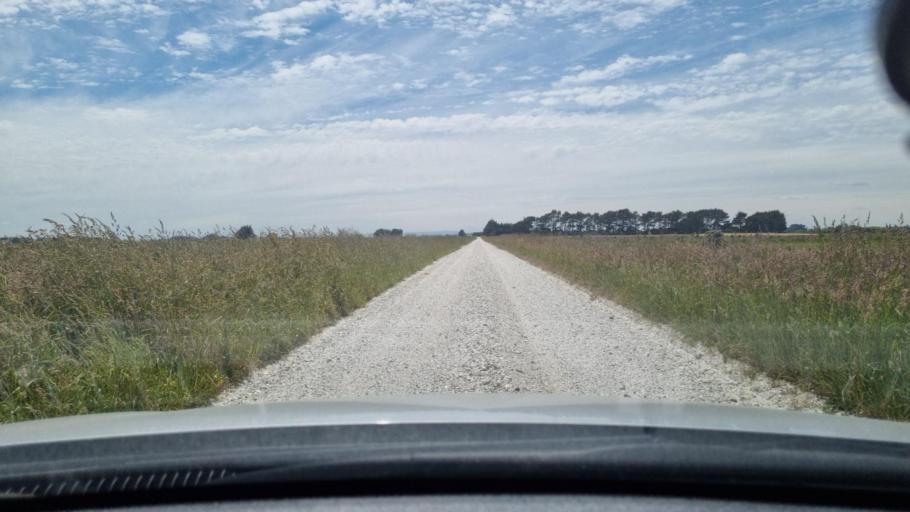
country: NZ
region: Southland
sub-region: Invercargill City
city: Invercargill
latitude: -46.3793
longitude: 168.2707
